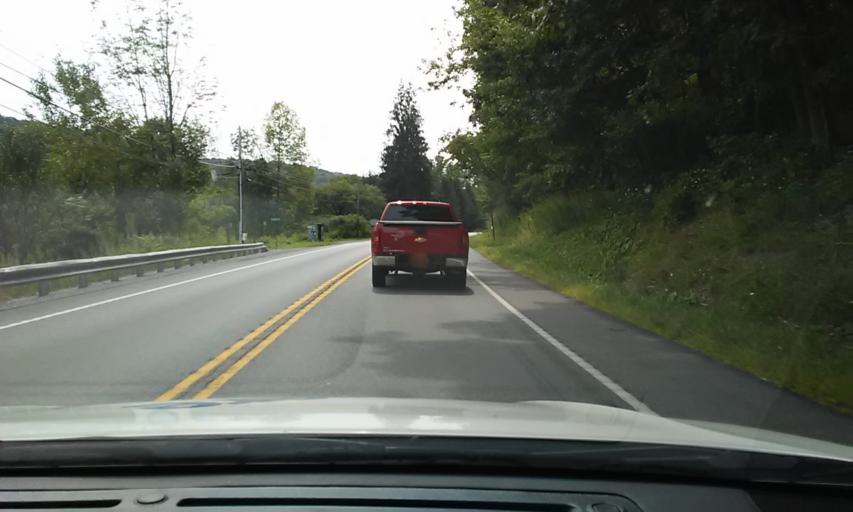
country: US
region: Pennsylvania
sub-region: Clearfield County
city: Treasure Lake
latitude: 41.1544
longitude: -78.6681
